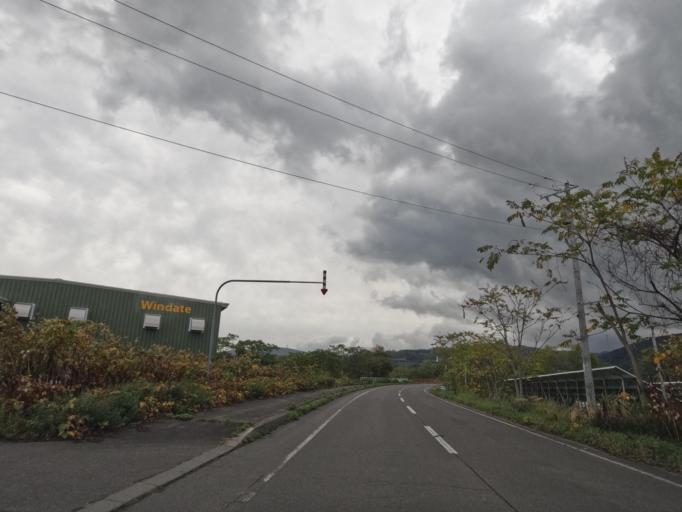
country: JP
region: Hokkaido
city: Date
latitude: 42.5052
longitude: 140.8759
